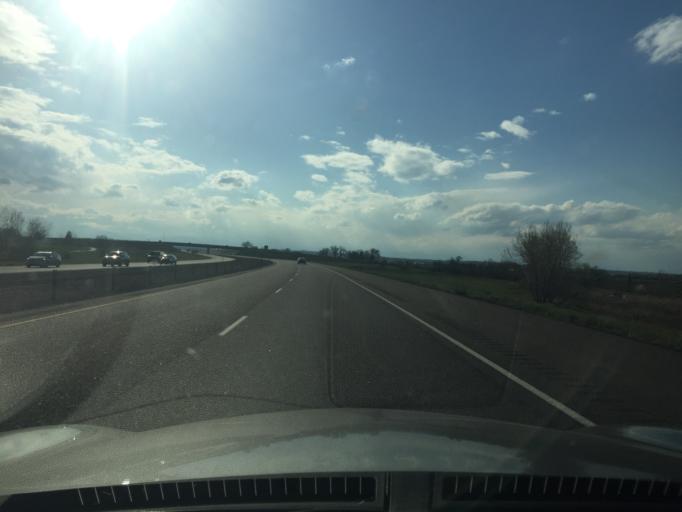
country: US
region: Colorado
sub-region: Adams County
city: Brighton
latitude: 39.9277
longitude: -104.8112
